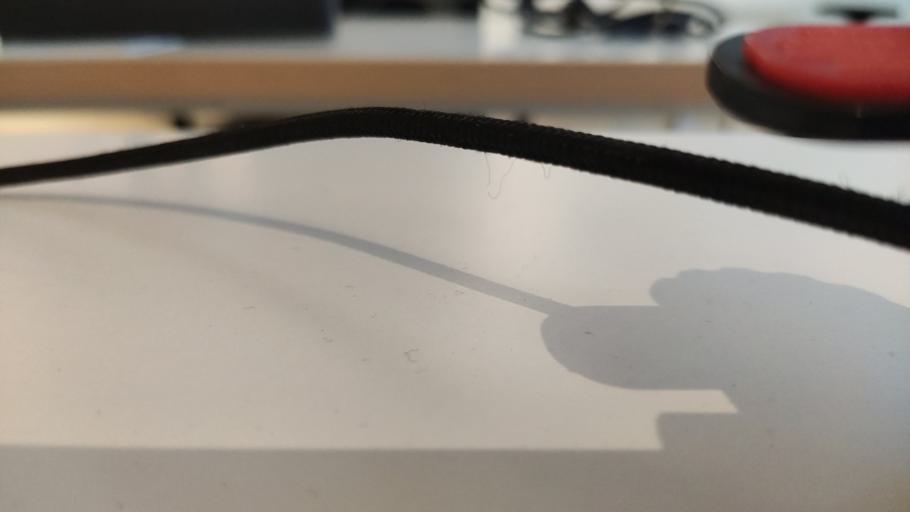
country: RU
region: Moskovskaya
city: Novopetrovskoye
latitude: 55.8691
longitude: 36.3967
